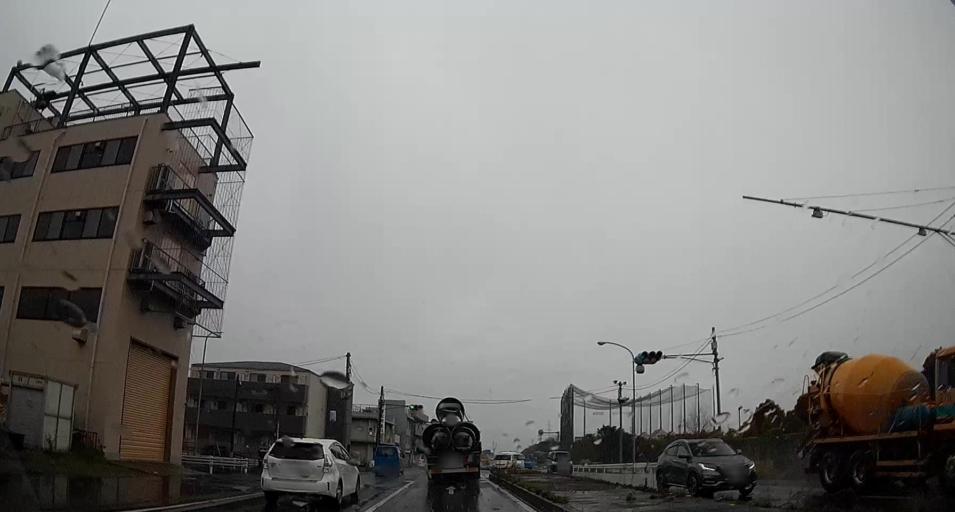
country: JP
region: Chiba
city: Chiba
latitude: 35.5789
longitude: 140.1272
